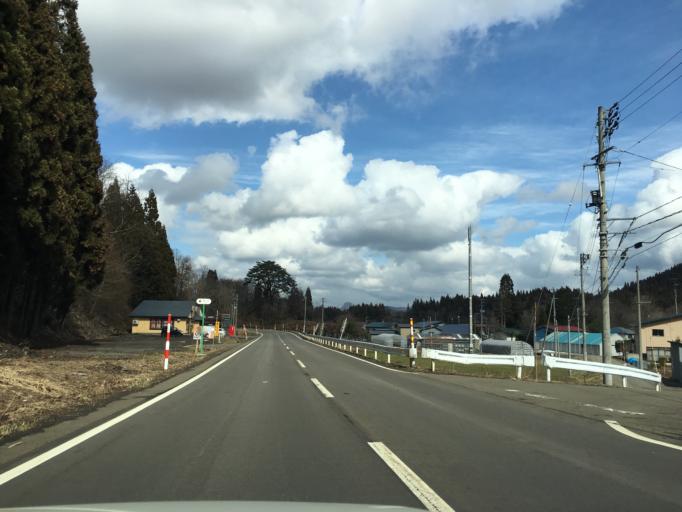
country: JP
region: Akita
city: Odate
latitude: 40.1950
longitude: 140.5337
